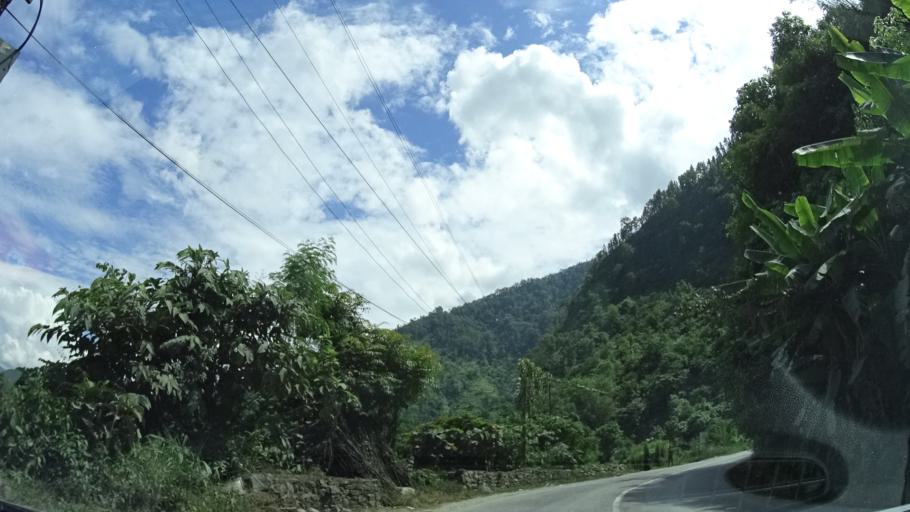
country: NP
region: Central Region
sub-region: Narayani Zone
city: Bharatpur
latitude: 27.7973
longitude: 84.7259
